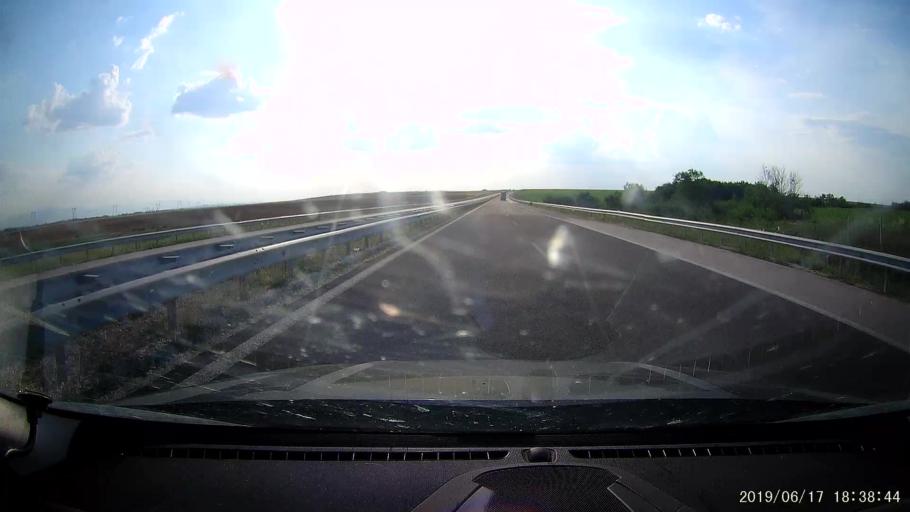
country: BG
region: Stara Zagora
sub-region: Obshtina Chirpan
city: Chirpan
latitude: 42.1389
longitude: 25.3284
